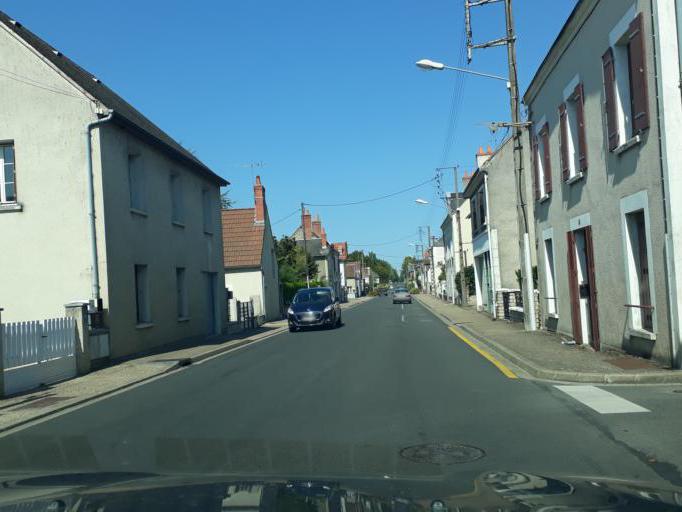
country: FR
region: Centre
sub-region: Departement de l'Indre
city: Chabris
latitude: 47.2565
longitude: 1.6548
